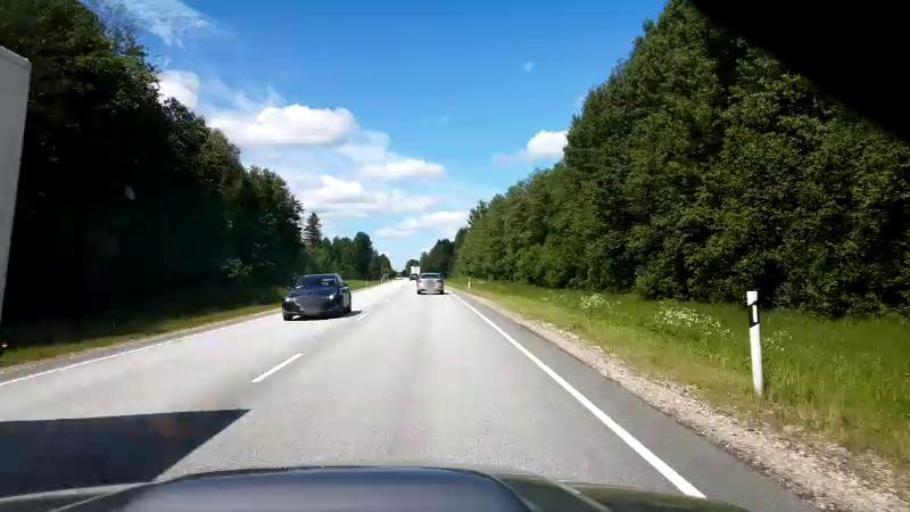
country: EE
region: Paernumaa
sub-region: Halinga vald
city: Parnu-Jaagupi
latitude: 58.5520
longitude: 24.5324
